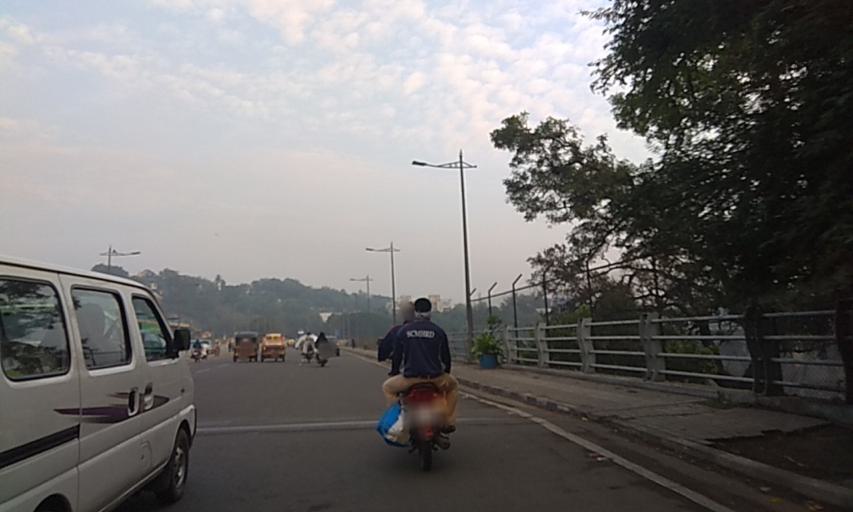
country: IN
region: Maharashtra
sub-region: Pune Division
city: Shivaji Nagar
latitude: 18.5418
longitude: 73.8840
